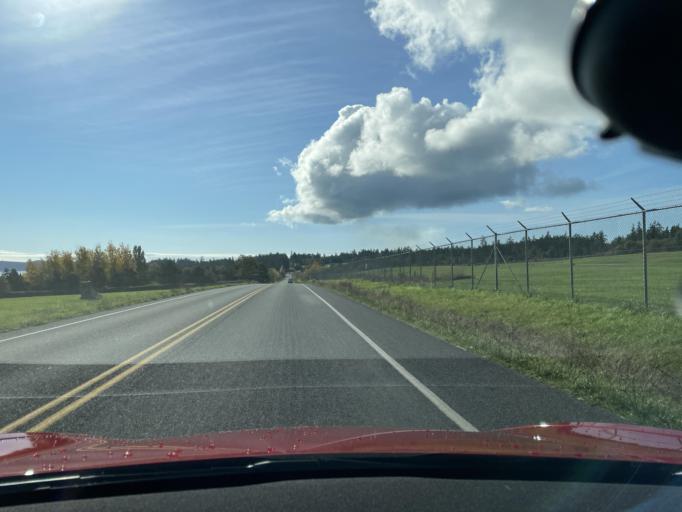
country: US
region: Washington
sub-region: San Juan County
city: Friday Harbor
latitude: 48.5194
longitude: -123.0231
